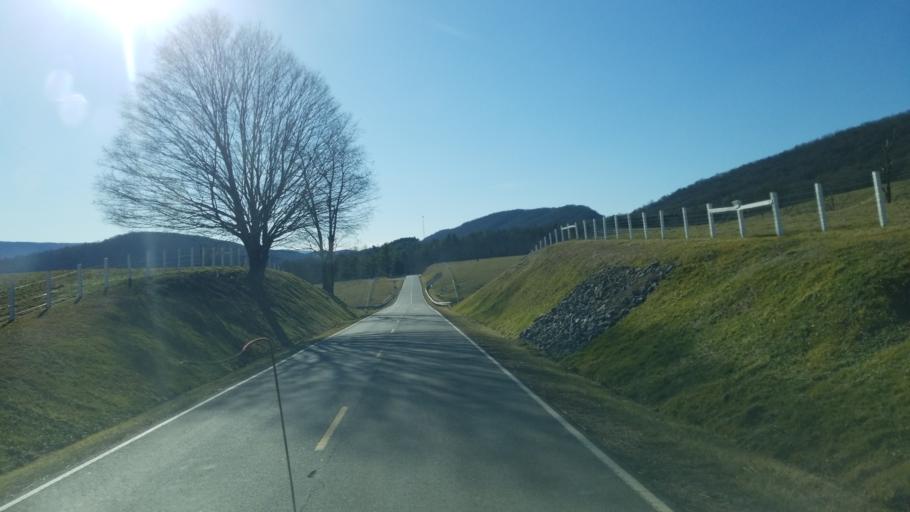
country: US
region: Virginia
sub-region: Pulaski County
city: Pulaski
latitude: 37.1753
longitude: -80.8811
